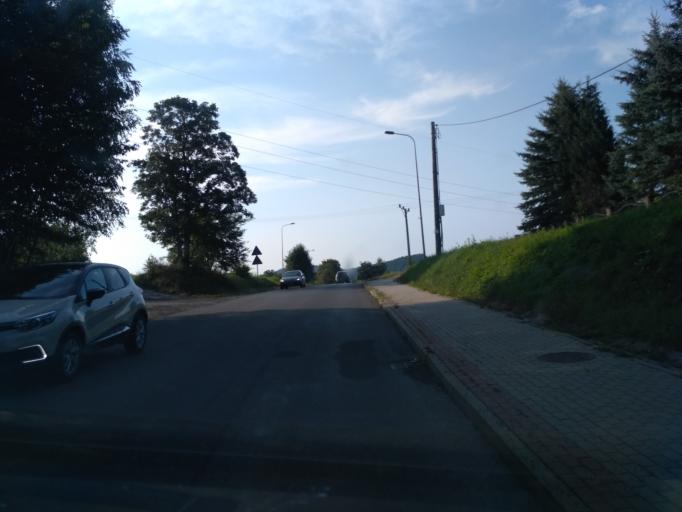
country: PL
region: Subcarpathian Voivodeship
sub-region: Powiat sanocki
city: Sanok
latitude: 49.5793
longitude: 22.1918
